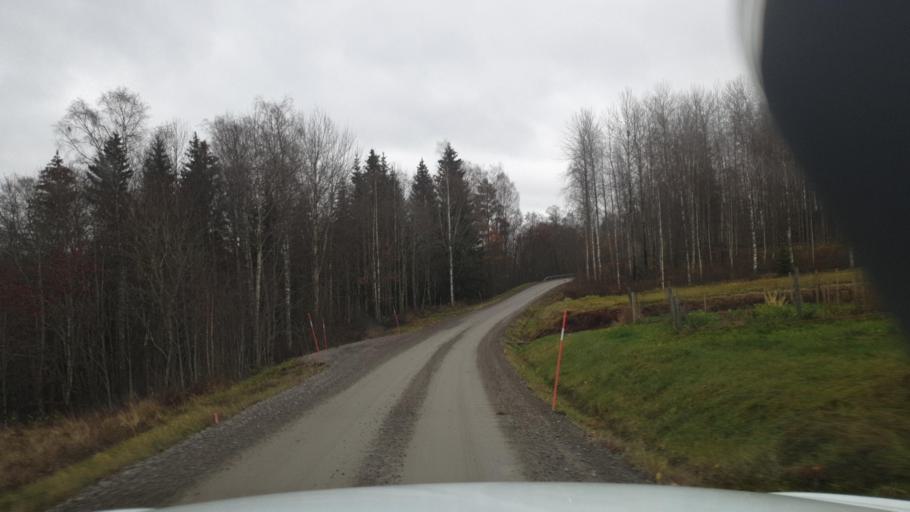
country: SE
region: Vaermland
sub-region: Arvika Kommun
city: Arvika
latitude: 59.8213
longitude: 12.5533
